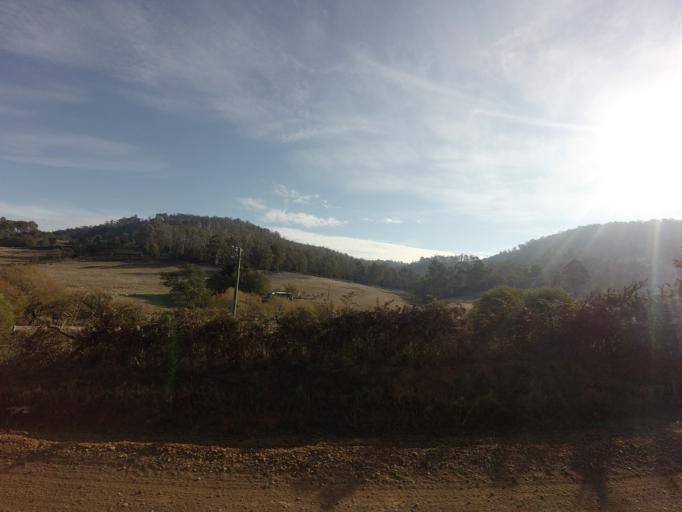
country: AU
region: Tasmania
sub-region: Sorell
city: Sorell
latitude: -42.4903
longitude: 147.4330
